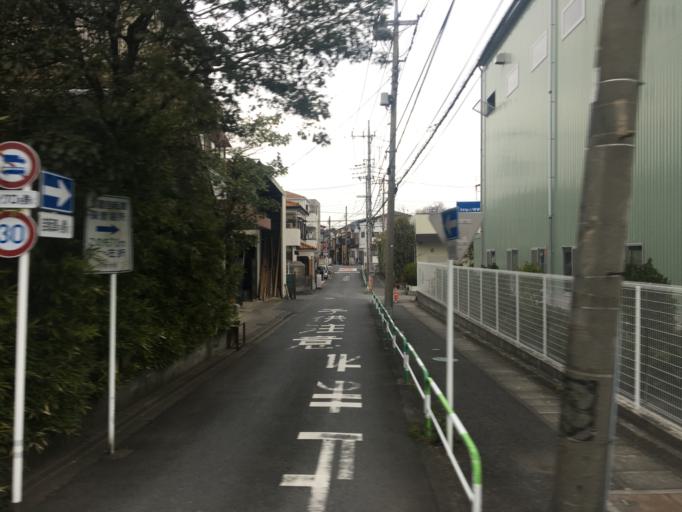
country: JP
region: Saitama
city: Shiki
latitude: 35.8427
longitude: 139.6211
